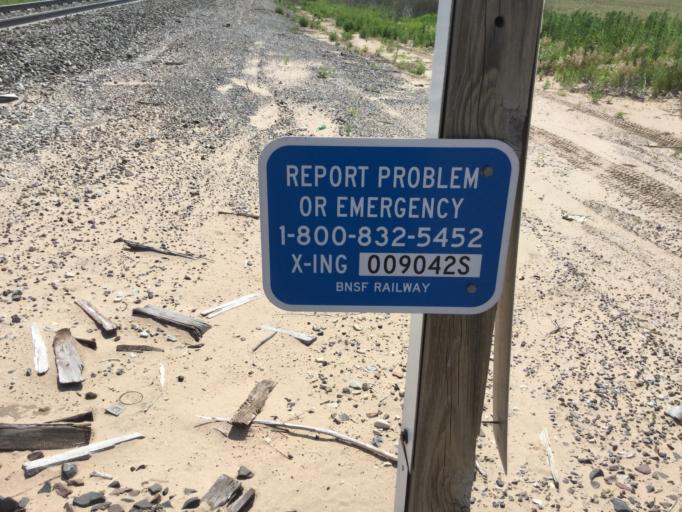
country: US
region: Kansas
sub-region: Pawnee County
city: Larned
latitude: 37.9500
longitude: -99.1323
